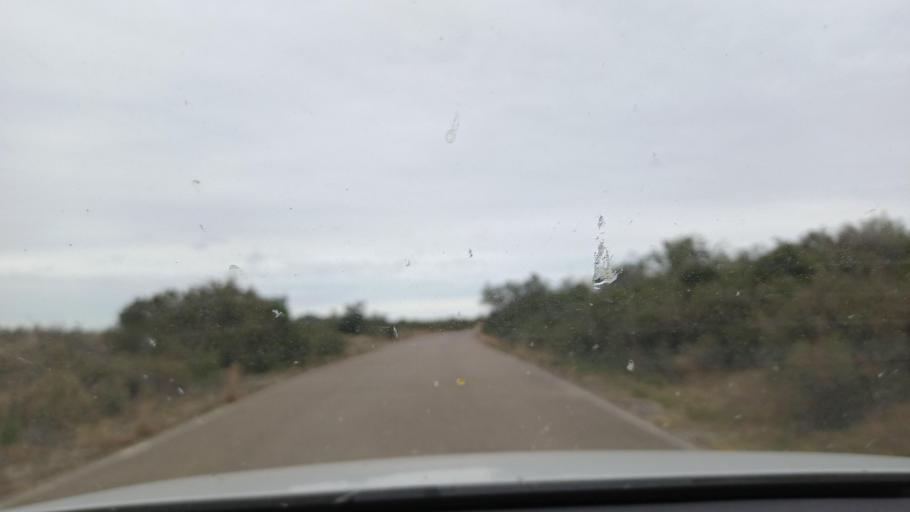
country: ES
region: Valencia
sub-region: Provincia de Castello
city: Canet lo Roig
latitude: 40.5892
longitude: 0.2821
